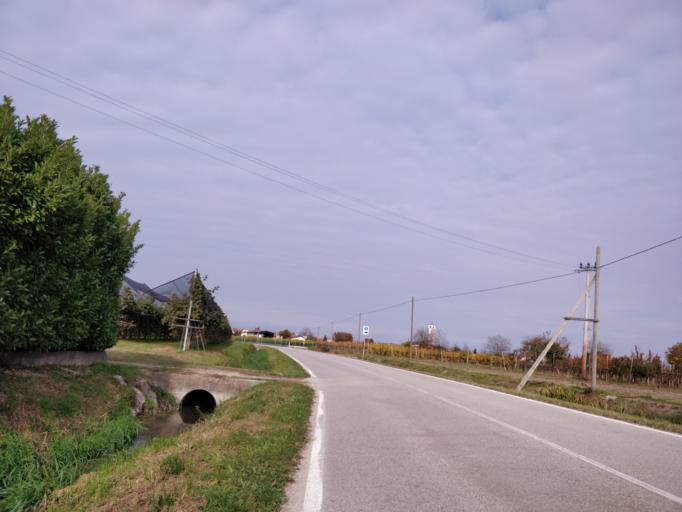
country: IT
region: Friuli Venezia Giulia
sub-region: Provincia di Udine
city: Bertiolo
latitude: 45.9367
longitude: 13.0508
